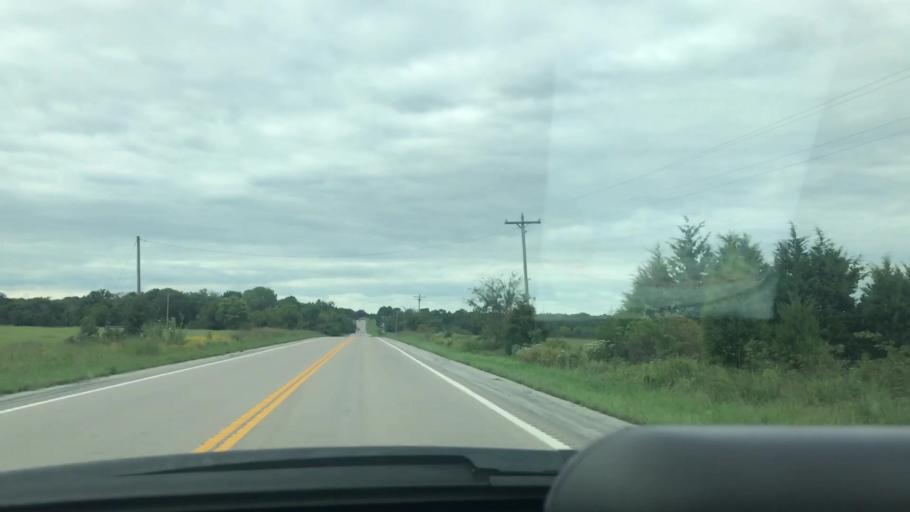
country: US
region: Missouri
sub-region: Benton County
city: Warsaw
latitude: 38.1448
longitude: -93.2901
